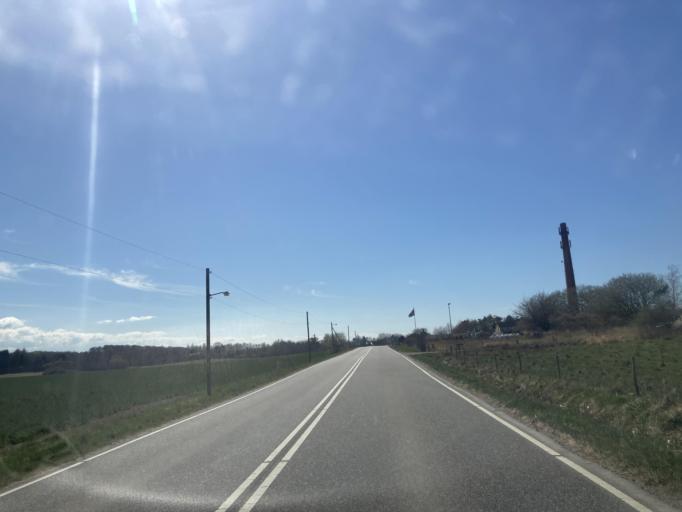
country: DK
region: Capital Region
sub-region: Gribskov Kommune
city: Graested
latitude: 56.0210
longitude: 12.2718
